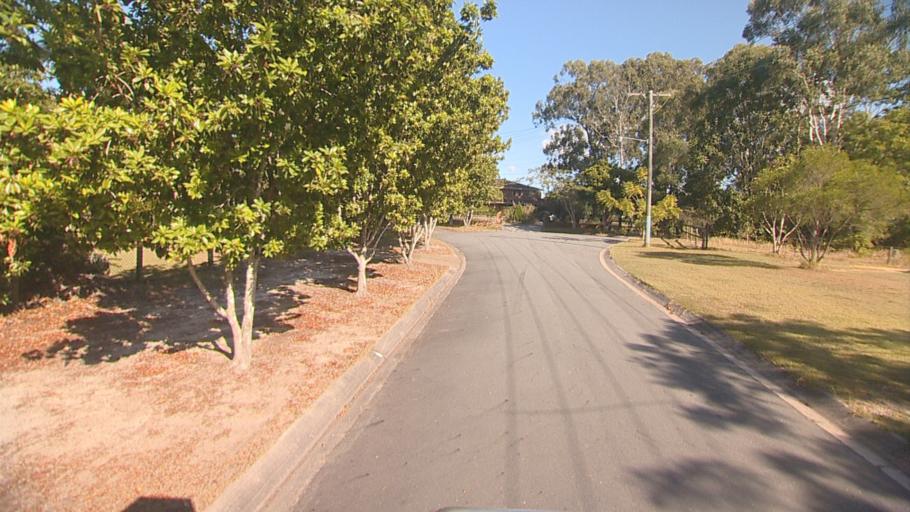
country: AU
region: Queensland
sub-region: Logan
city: Park Ridge South
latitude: -27.7068
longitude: 153.0175
